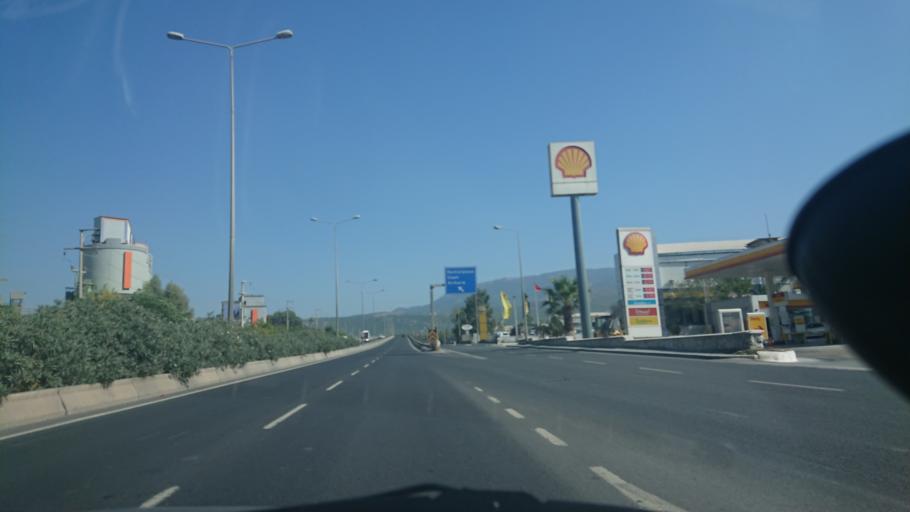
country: TR
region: Izmir
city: Bornova
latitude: 38.4541
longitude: 27.2611
